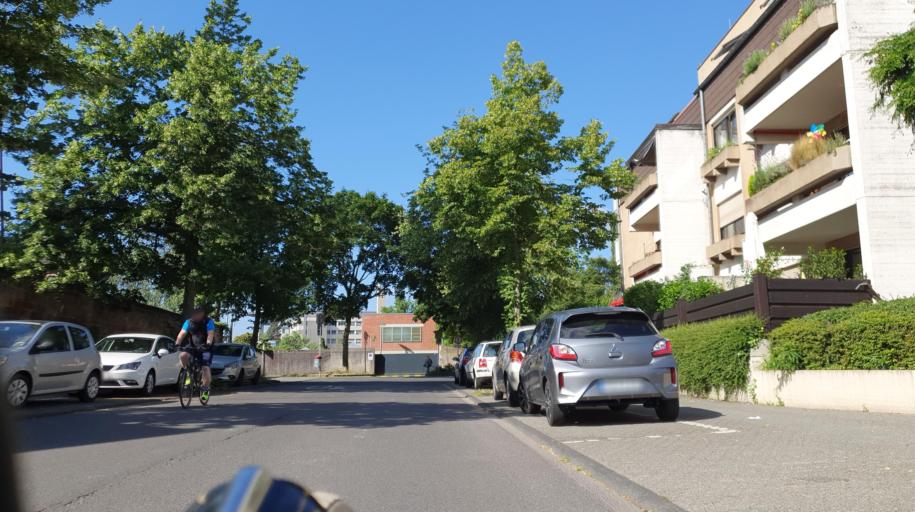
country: DE
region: Rheinland-Pfalz
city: Trier
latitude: 49.7647
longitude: 6.6438
